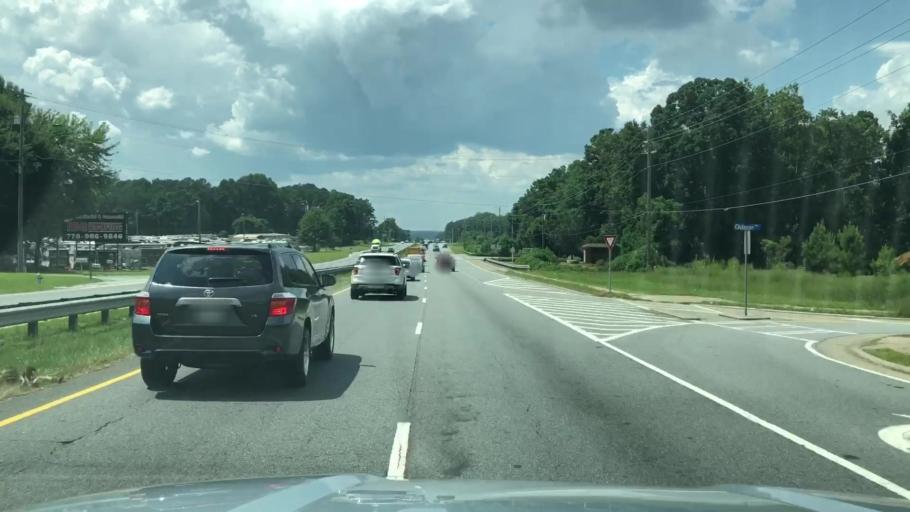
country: US
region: Georgia
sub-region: Cobb County
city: Kennesaw
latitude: 34.0281
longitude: -84.6433
